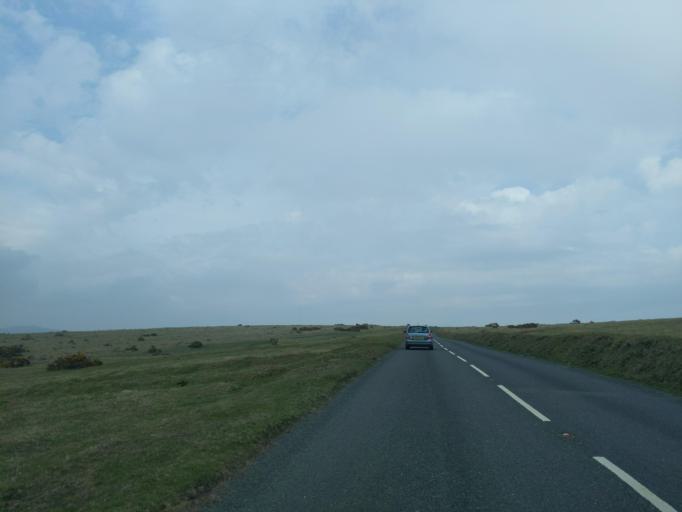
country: GB
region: England
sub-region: Devon
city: Yelverton
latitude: 50.5154
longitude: -4.0409
